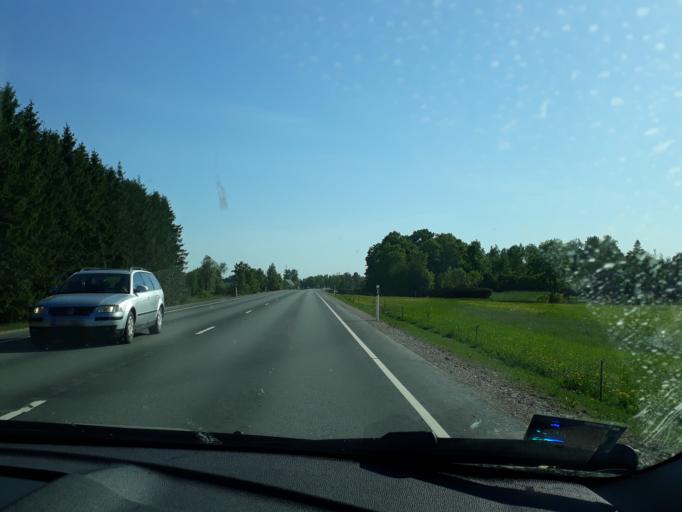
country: EE
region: Paernumaa
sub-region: Tootsi vald
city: Tootsi
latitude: 58.5414
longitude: 24.8414
